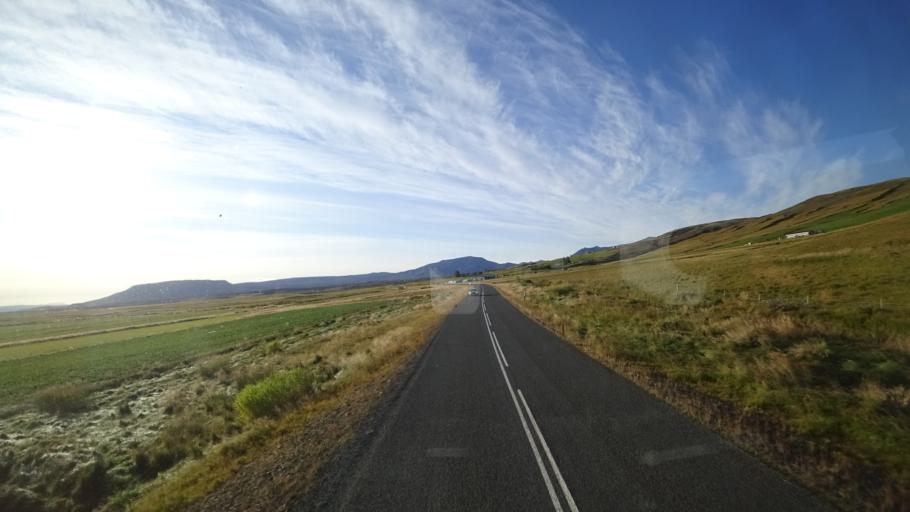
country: IS
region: South
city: Selfoss
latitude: 64.2718
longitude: -20.3884
